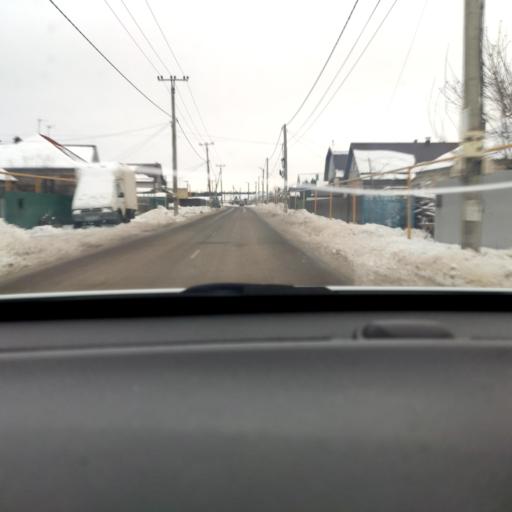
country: RU
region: Voronezj
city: Somovo
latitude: 51.7537
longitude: 39.4368
